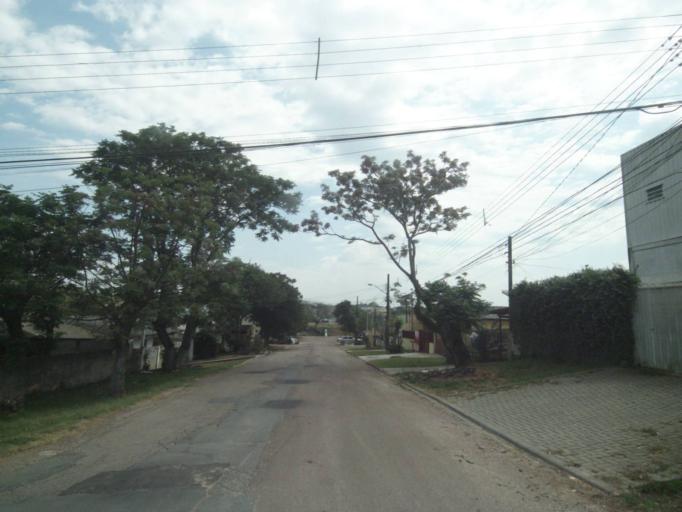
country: BR
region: Parana
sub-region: Sao Jose Dos Pinhais
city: Sao Jose dos Pinhais
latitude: -25.5268
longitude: -49.2621
